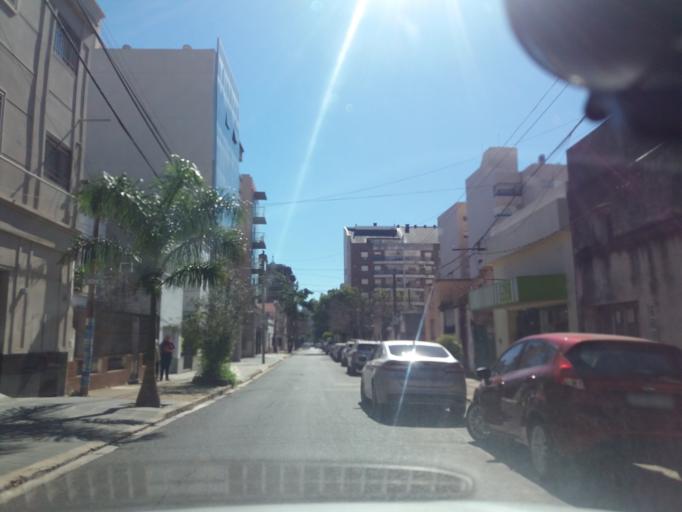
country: AR
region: Corrientes
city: Corrientes
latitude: -27.4690
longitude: -58.8431
